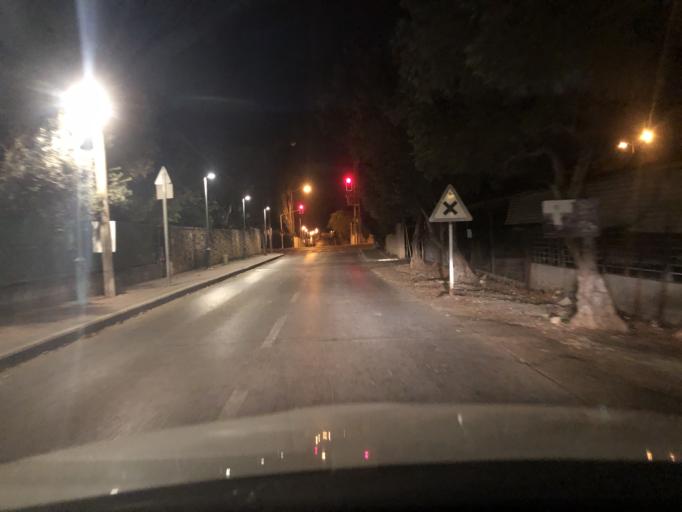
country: IL
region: Central District
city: Hod HaSharon
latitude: 32.1679
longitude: 34.8944
